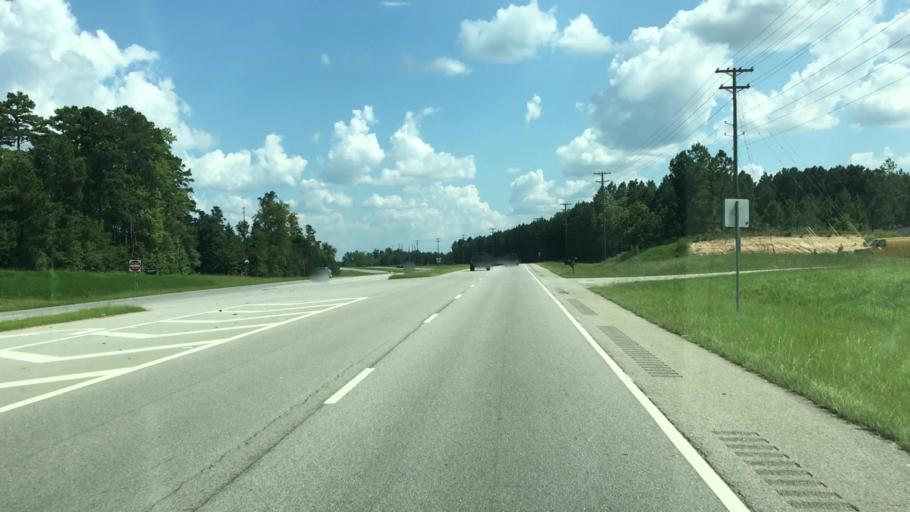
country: US
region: Georgia
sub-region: Putnam County
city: Eatonton
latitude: 33.2191
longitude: -83.3066
